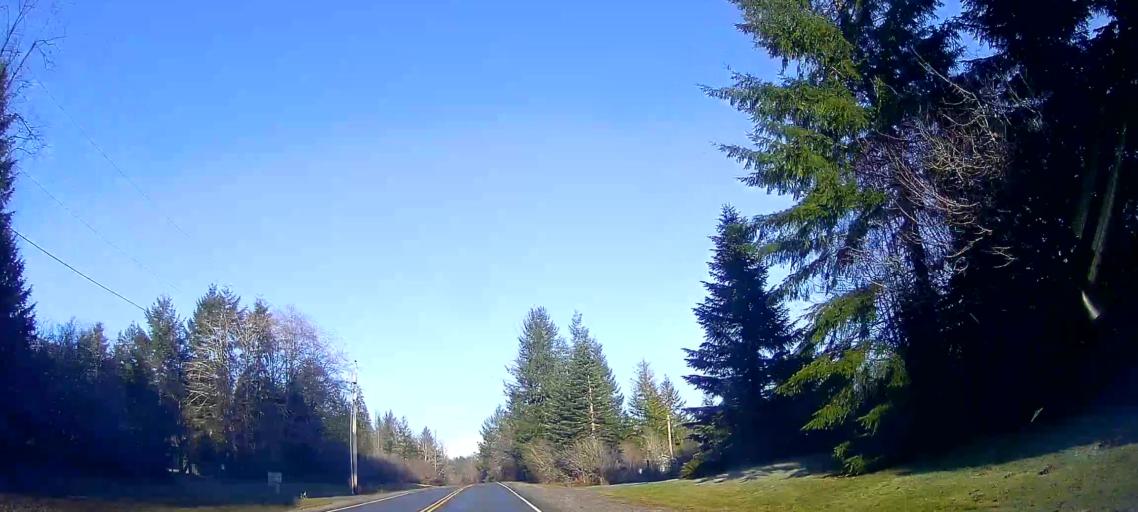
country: US
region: Washington
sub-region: Snohomish County
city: Darrington
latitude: 48.5928
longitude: -121.7712
